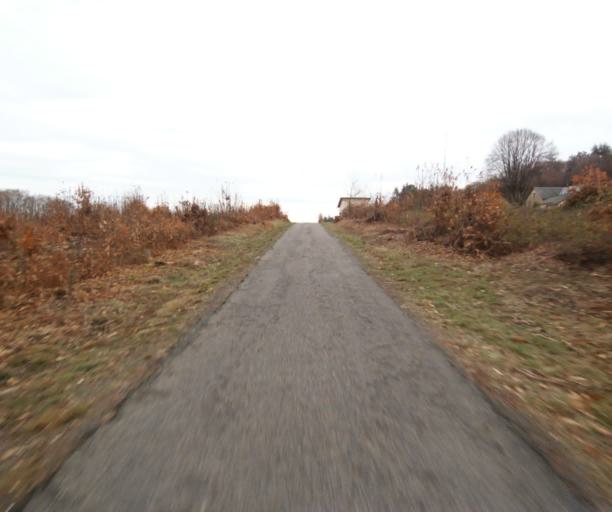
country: FR
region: Limousin
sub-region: Departement de la Correze
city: Chameyrat
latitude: 45.2351
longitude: 1.6614
